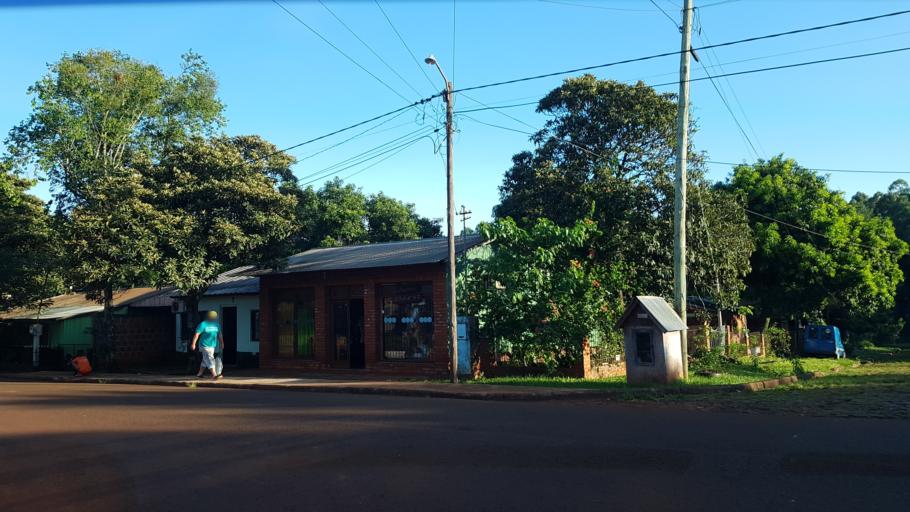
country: AR
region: Misiones
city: Puerto Libertad
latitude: -25.9238
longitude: -54.5833
